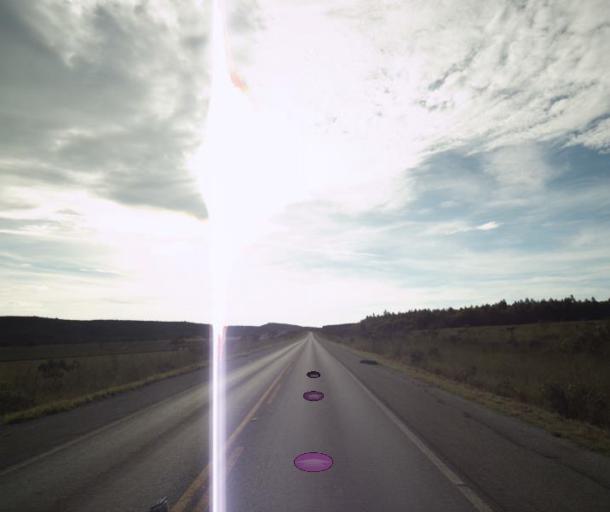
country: BR
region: Goias
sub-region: Pirenopolis
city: Pirenopolis
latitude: -15.7507
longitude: -48.6185
